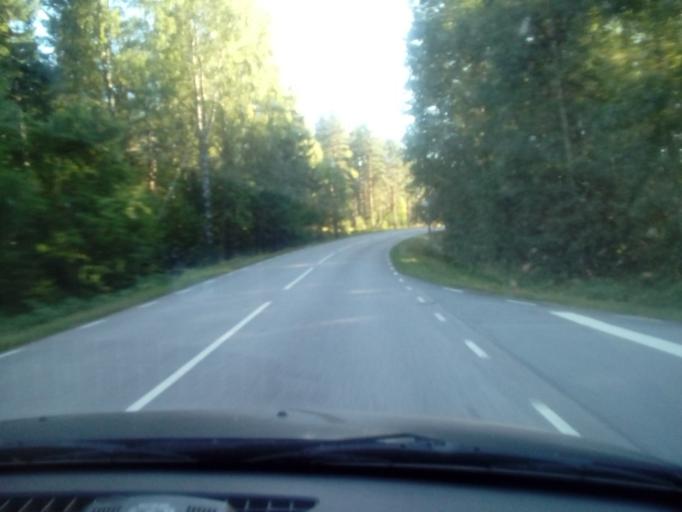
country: SE
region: Kalmar
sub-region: Vasterviks Kommun
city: Gamleby
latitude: 57.8194
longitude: 16.4526
